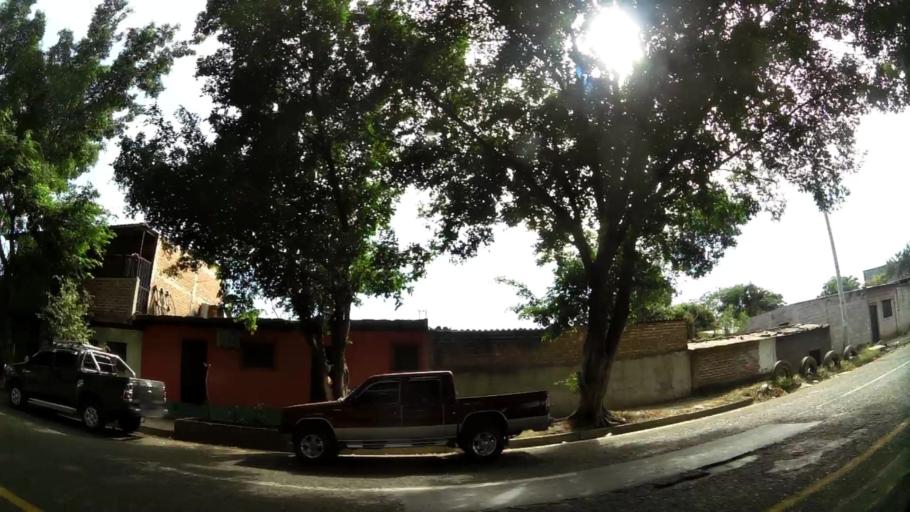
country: SV
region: Santa Ana
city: Chalchuapa
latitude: 13.9881
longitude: -89.6740
